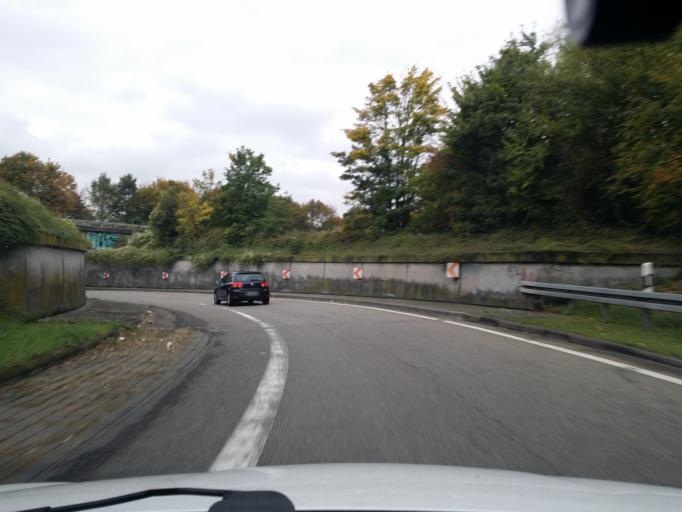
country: DE
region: Hesse
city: Sulzbach
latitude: 50.1153
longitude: 8.5309
